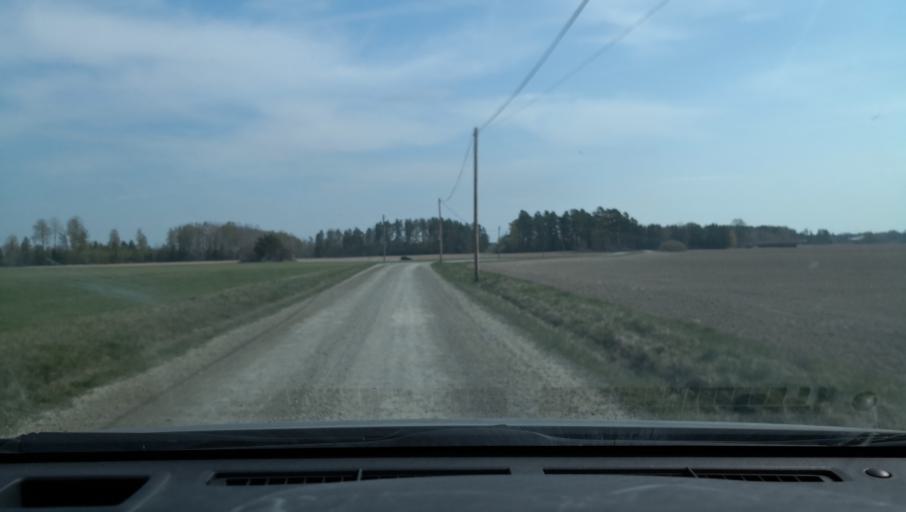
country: SE
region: Vaestmanland
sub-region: Vasteras
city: Skultuna
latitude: 59.7904
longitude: 16.4486
